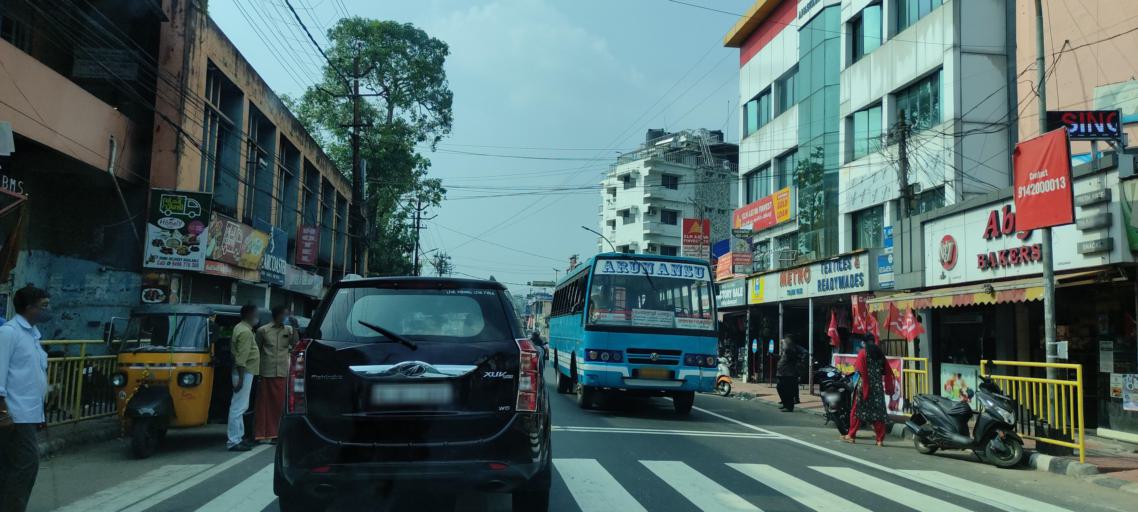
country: IN
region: Kerala
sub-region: Alappuzha
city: Chengannur
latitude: 9.3186
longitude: 76.6132
